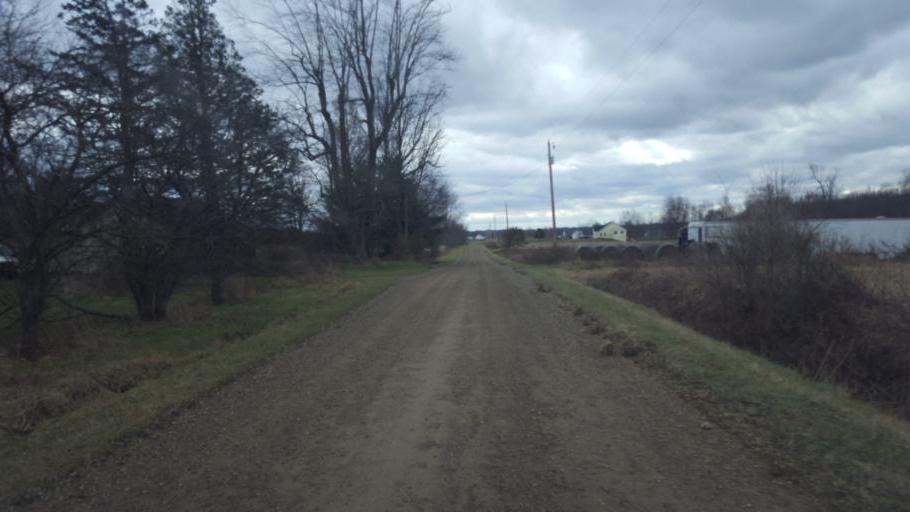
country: US
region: Ohio
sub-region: Licking County
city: Utica
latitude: 40.2810
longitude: -82.4978
